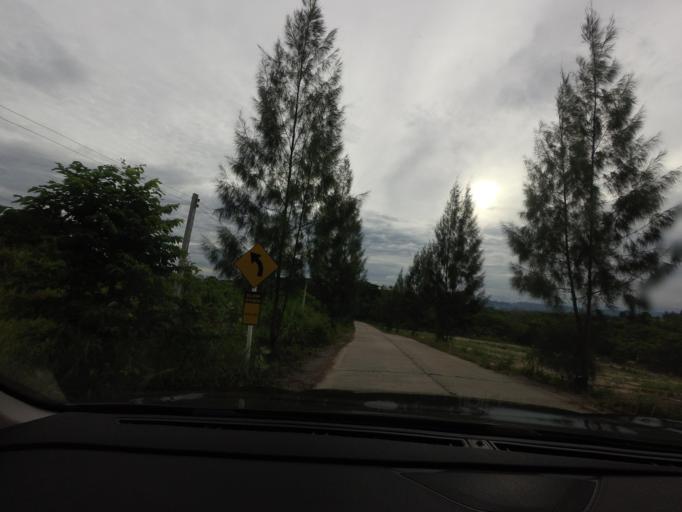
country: TH
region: Prachuap Khiri Khan
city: Hua Hin
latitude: 12.4818
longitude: 99.9390
